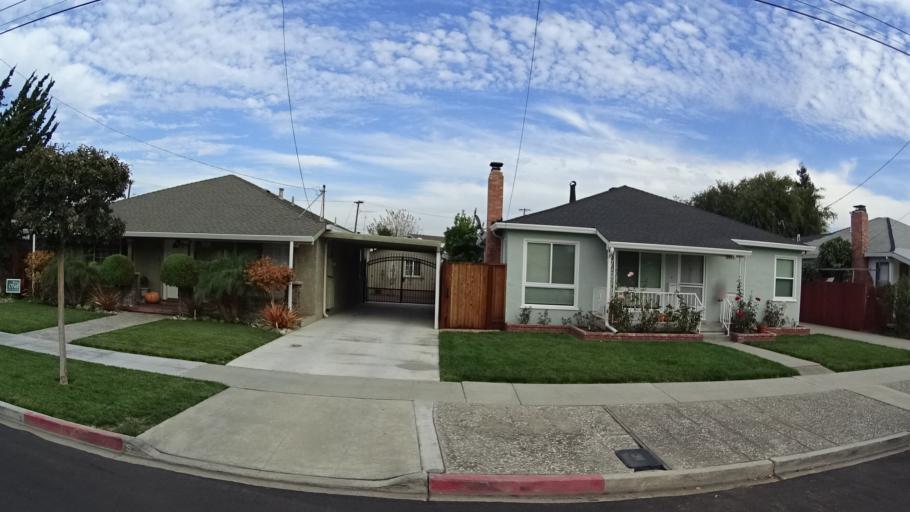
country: US
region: California
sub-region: Santa Clara County
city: Santa Clara
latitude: 37.3584
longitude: -121.9508
